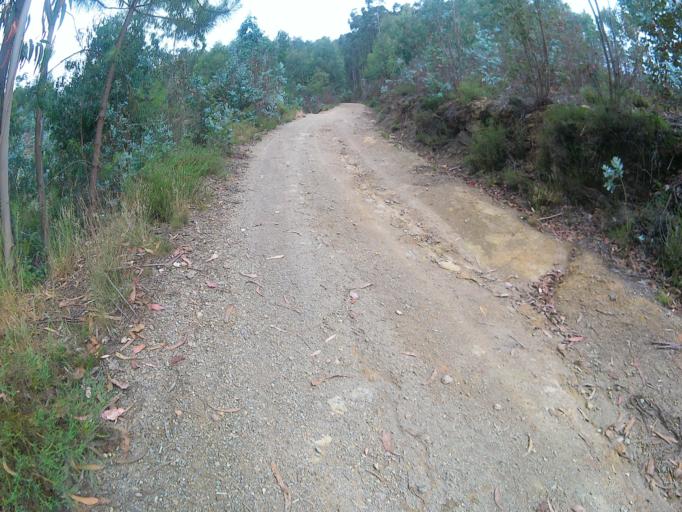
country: PT
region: Aveiro
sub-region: Albergaria-A-Velha
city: Branca
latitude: 40.7577
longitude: -8.4281
